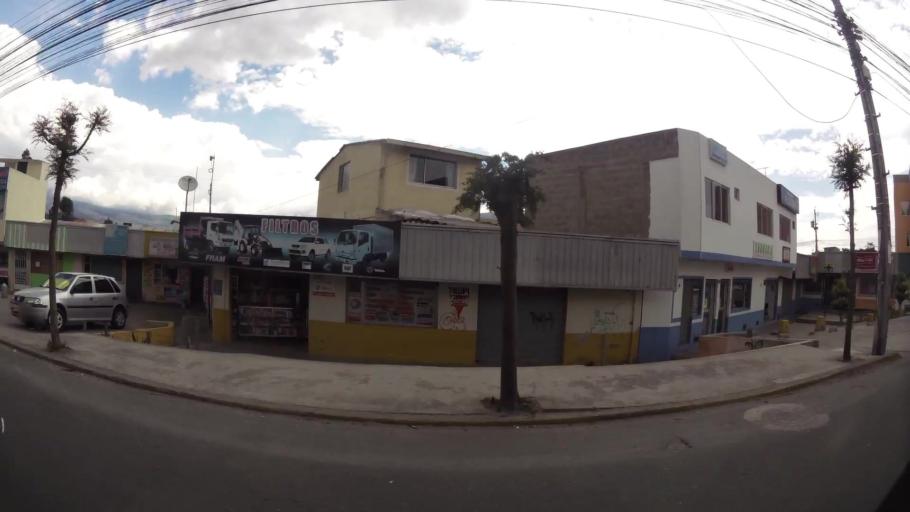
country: EC
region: Pichincha
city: Quito
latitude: -0.0870
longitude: -78.4386
